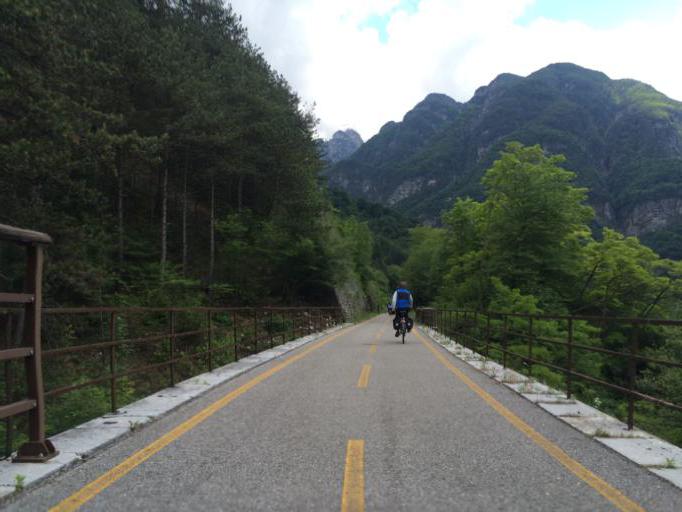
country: IT
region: Friuli Venezia Giulia
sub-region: Provincia di Udine
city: Dogna
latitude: 46.4556
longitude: 13.3125
